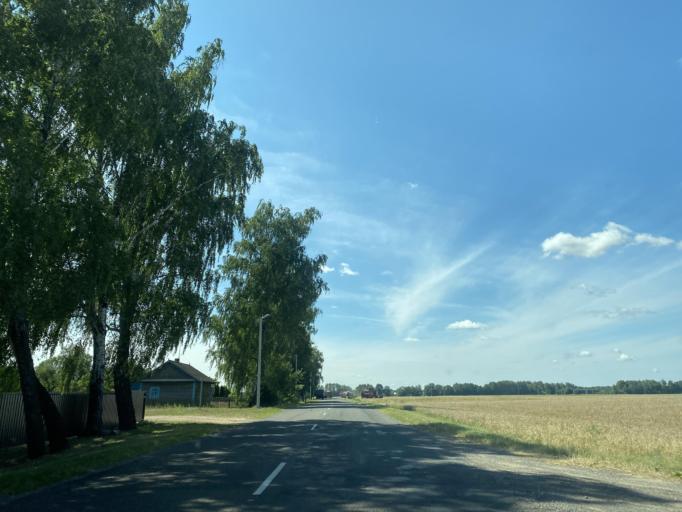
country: BY
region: Brest
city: Ivanava
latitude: 52.1985
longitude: 25.6136
